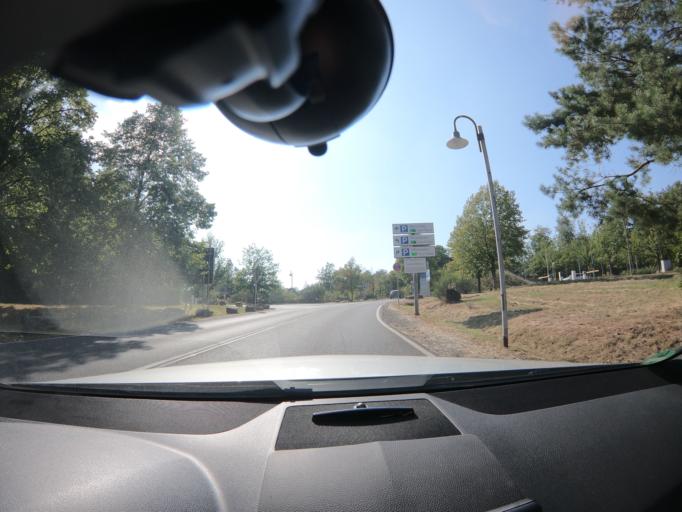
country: DE
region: Hesse
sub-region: Regierungsbezirk Giessen
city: Colbe
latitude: 50.8176
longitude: 8.8089
